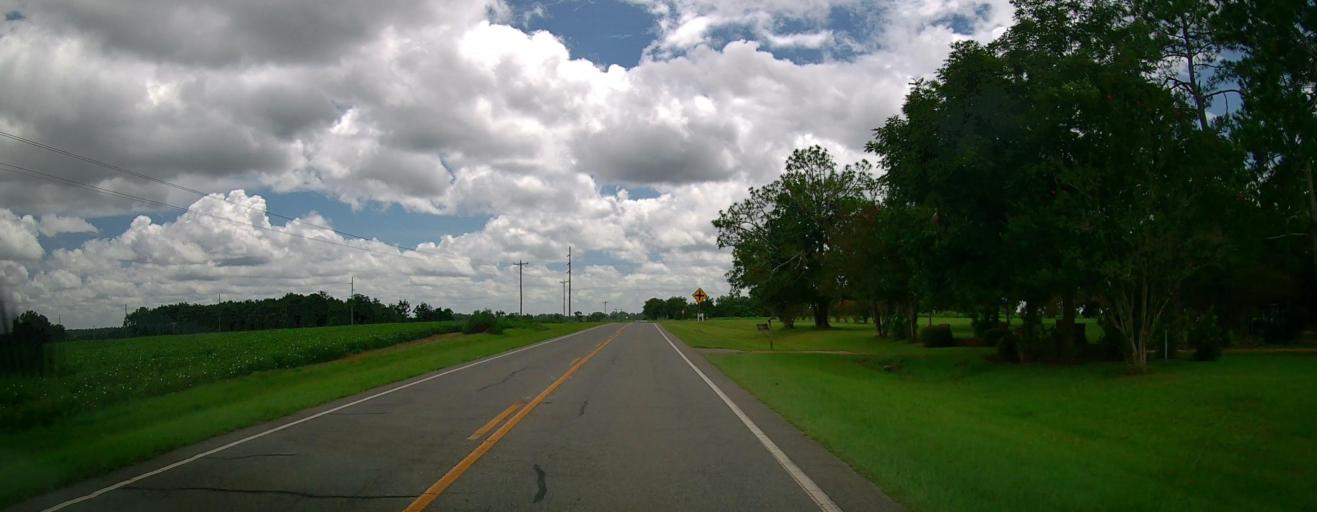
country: US
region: Georgia
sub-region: Wilcox County
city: Rochelle
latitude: 31.9824
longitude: -83.5455
